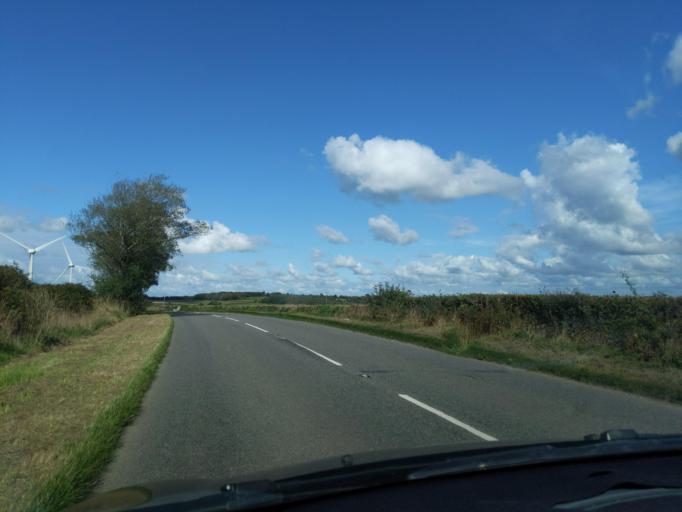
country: GB
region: England
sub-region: Cornwall
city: Boyton
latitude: 50.7378
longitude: -4.3230
